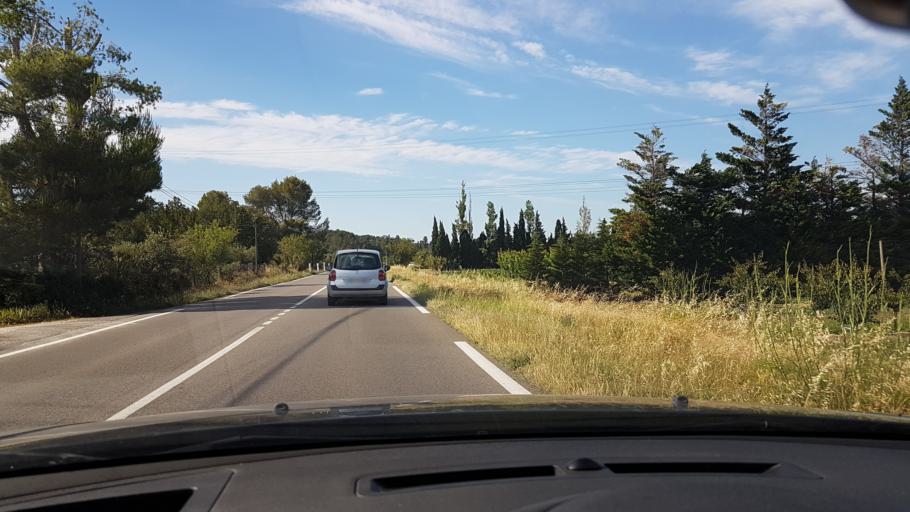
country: FR
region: Provence-Alpes-Cote d'Azur
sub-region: Departement des Bouches-du-Rhone
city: Graveson
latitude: 43.8639
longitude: 4.7697
